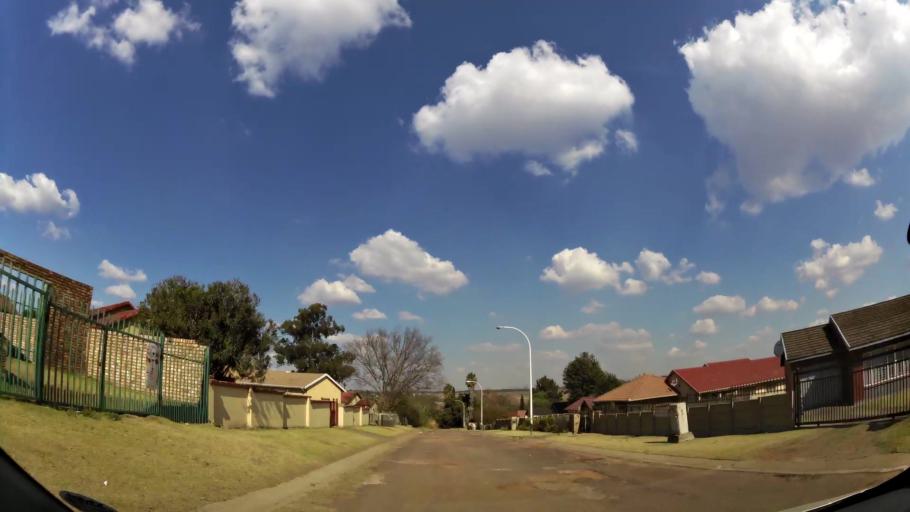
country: ZA
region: Mpumalanga
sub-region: Nkangala District Municipality
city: Witbank
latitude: -25.9283
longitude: 29.2365
